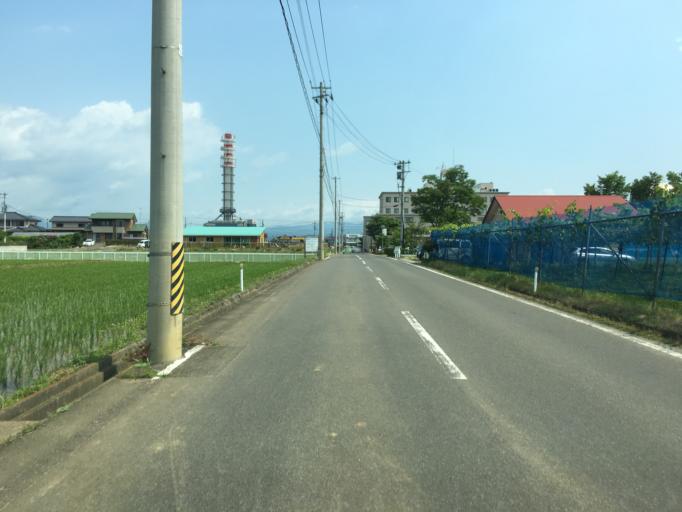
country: JP
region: Fukushima
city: Fukushima-shi
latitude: 37.7381
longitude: 140.4438
